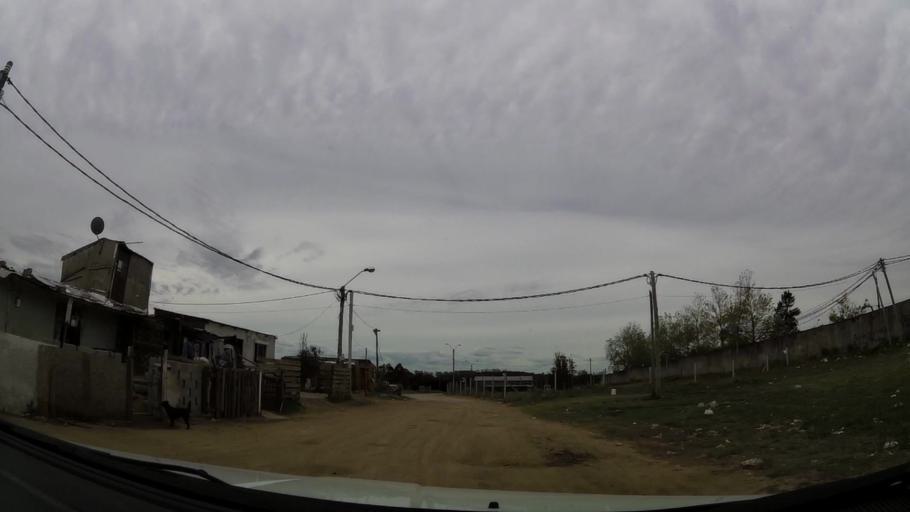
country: UY
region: Maldonado
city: Maldonado
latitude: -34.8837
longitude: -54.9551
